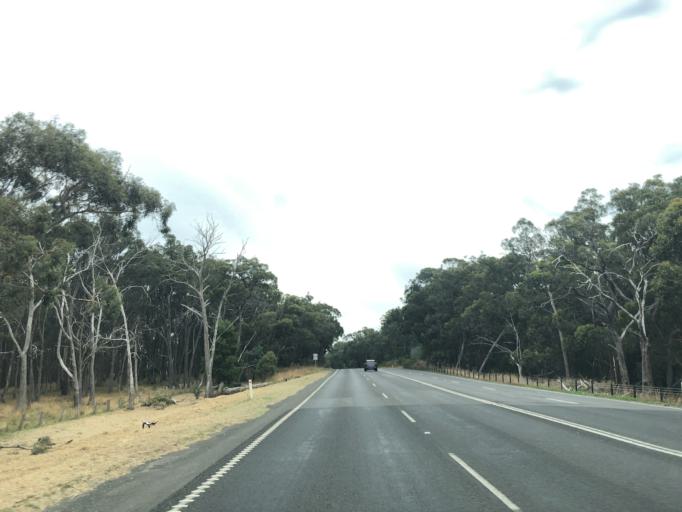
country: AU
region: Victoria
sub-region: Hume
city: Sunbury
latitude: -37.3727
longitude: 144.5264
